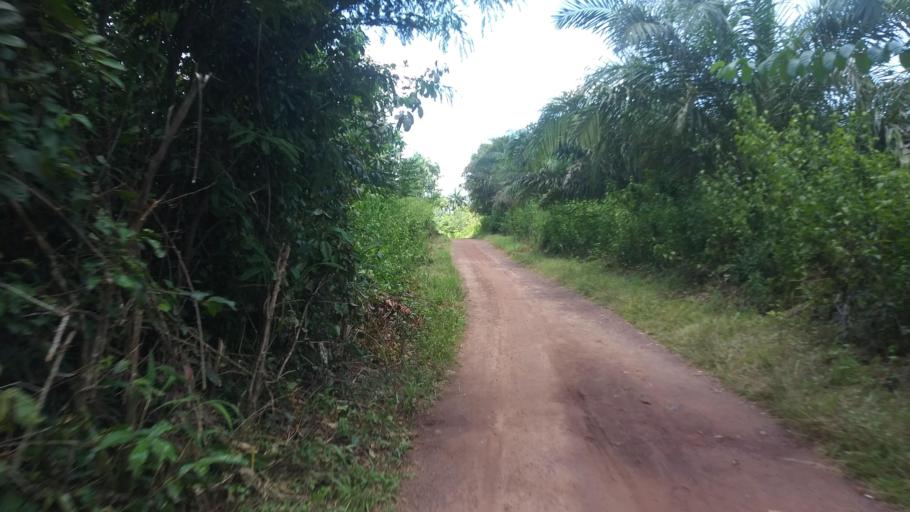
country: SL
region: Northern Province
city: Makeni
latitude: 8.8991
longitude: -11.9950
